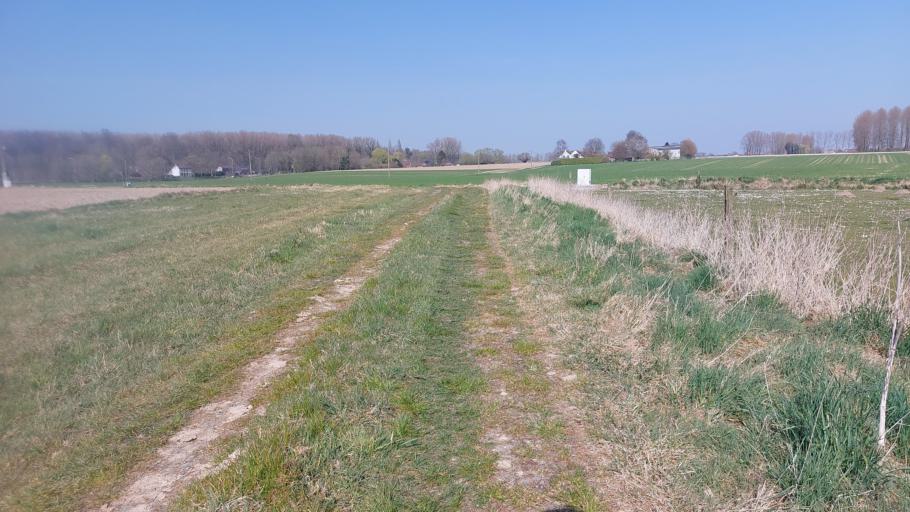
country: BE
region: Wallonia
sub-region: Province du Hainaut
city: Soignies
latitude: 50.5321
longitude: 4.0383
